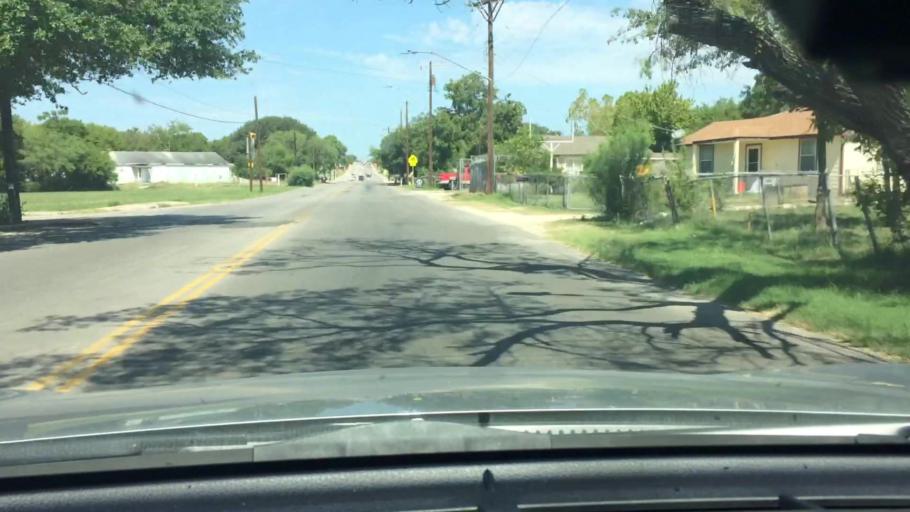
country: US
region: Texas
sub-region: Bexar County
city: San Antonio
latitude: 29.3965
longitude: -98.4339
